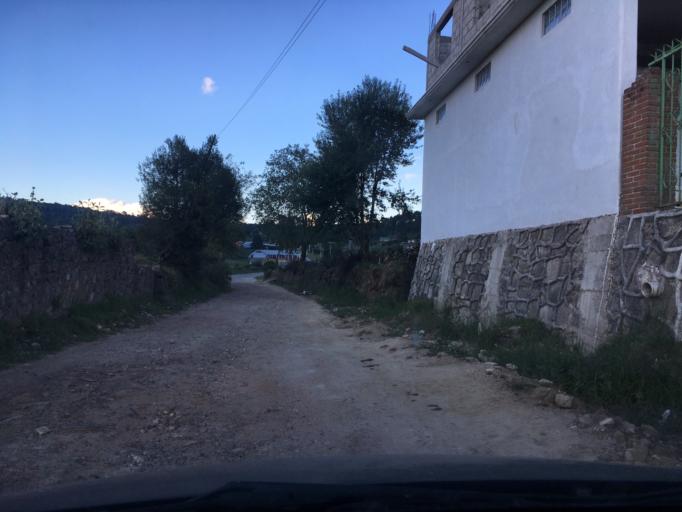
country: MX
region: Hidalgo
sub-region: Omitlan de Juarez
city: San Antonio el Paso
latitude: 20.1458
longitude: -98.6140
